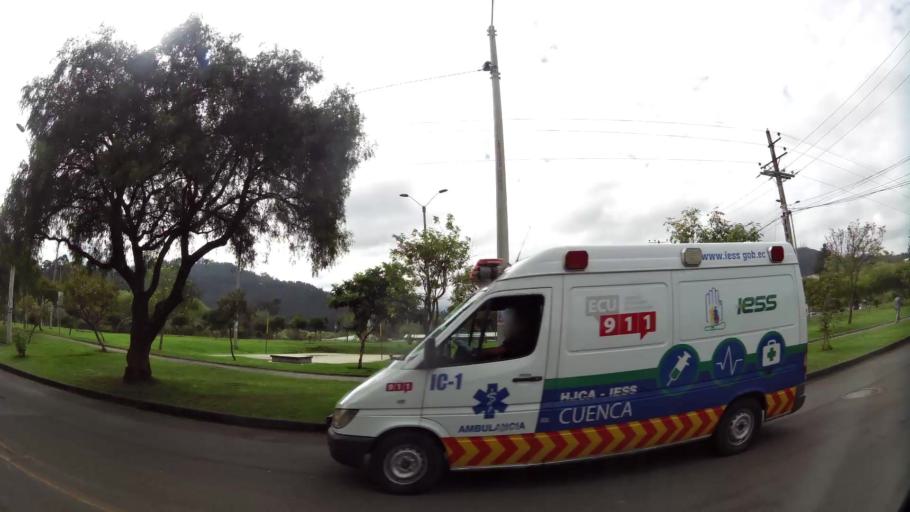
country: EC
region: Azuay
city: Cuenca
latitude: -2.9080
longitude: -78.9904
